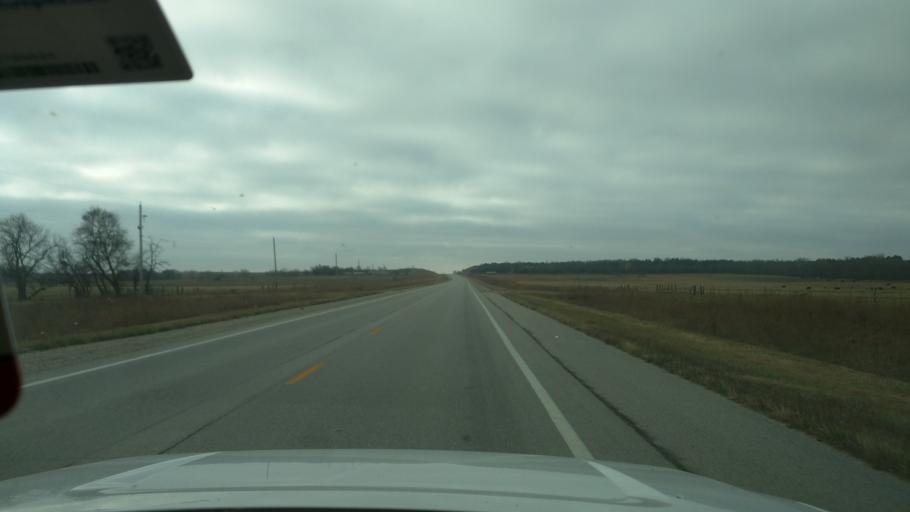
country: US
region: Kansas
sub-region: Elk County
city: Howard
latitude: 37.6146
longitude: -96.2533
